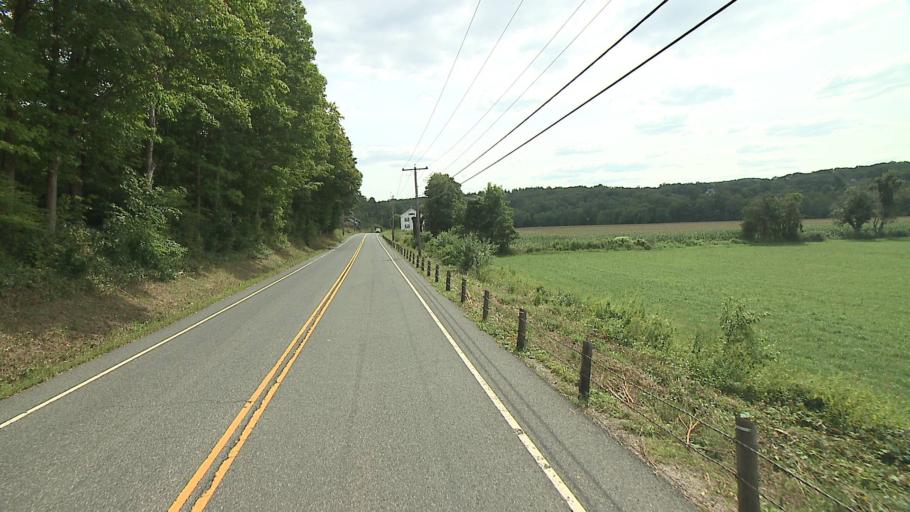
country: US
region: Connecticut
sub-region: Litchfield County
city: Woodbury
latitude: 41.5840
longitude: -73.2304
